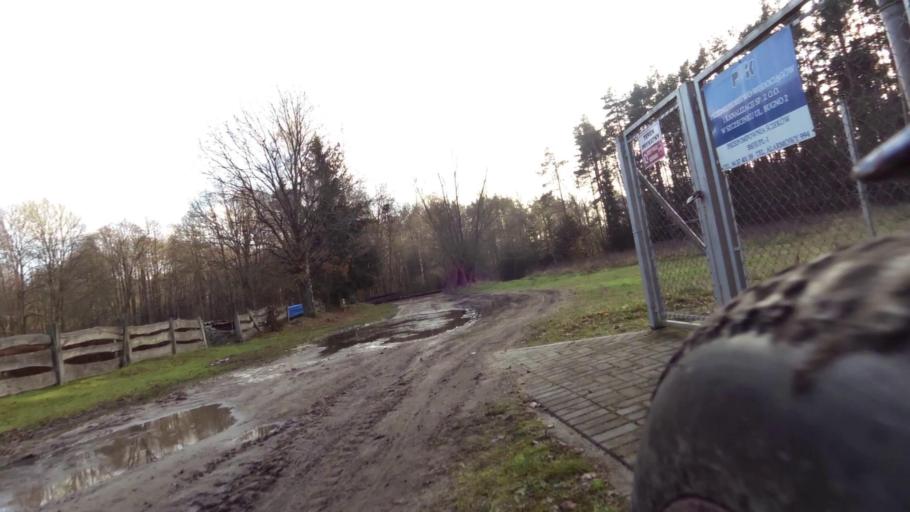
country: PL
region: West Pomeranian Voivodeship
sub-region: Powiat szczecinecki
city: Borne Sulinowo
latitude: 53.6151
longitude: 16.6208
